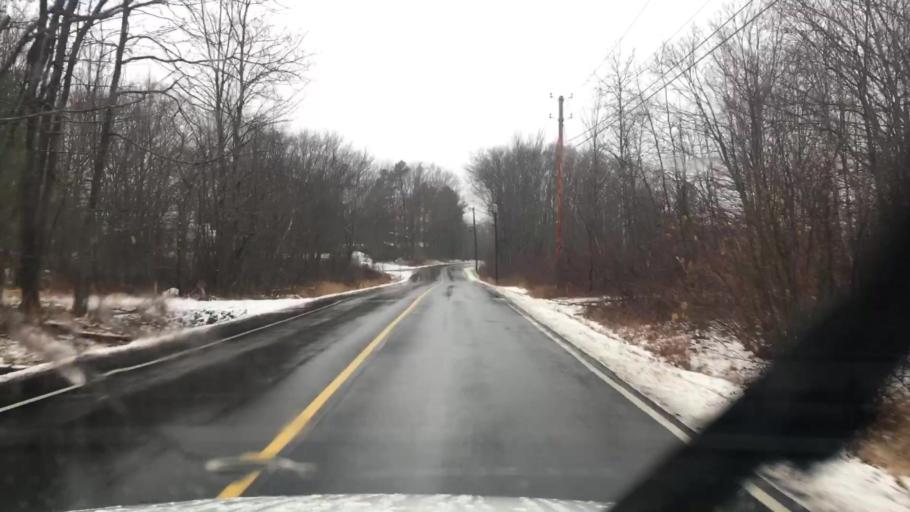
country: US
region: Maine
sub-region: York County
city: Arundel
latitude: 43.4104
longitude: -70.4129
